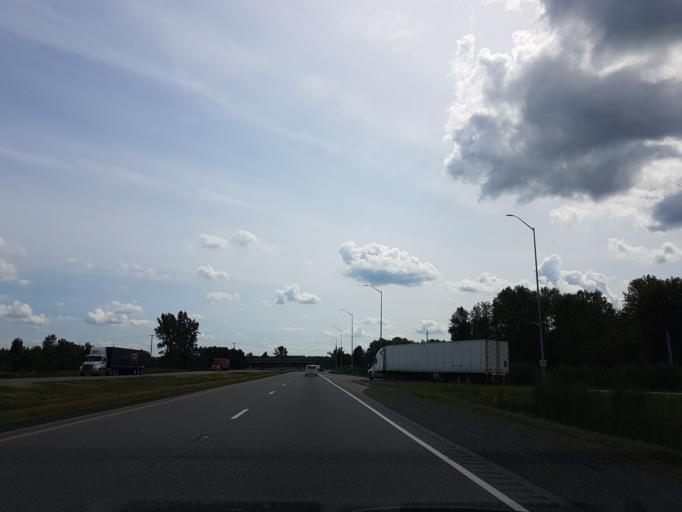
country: US
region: New York
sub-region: St. Lawrence County
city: Norfolk
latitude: 44.9700
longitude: -75.0806
